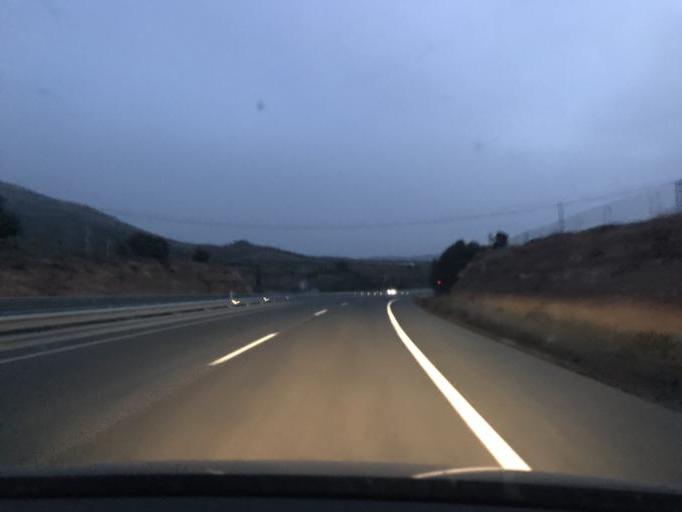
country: ES
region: Andalusia
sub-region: Provincia de Granada
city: Gor
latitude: 37.4094
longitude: -2.9191
